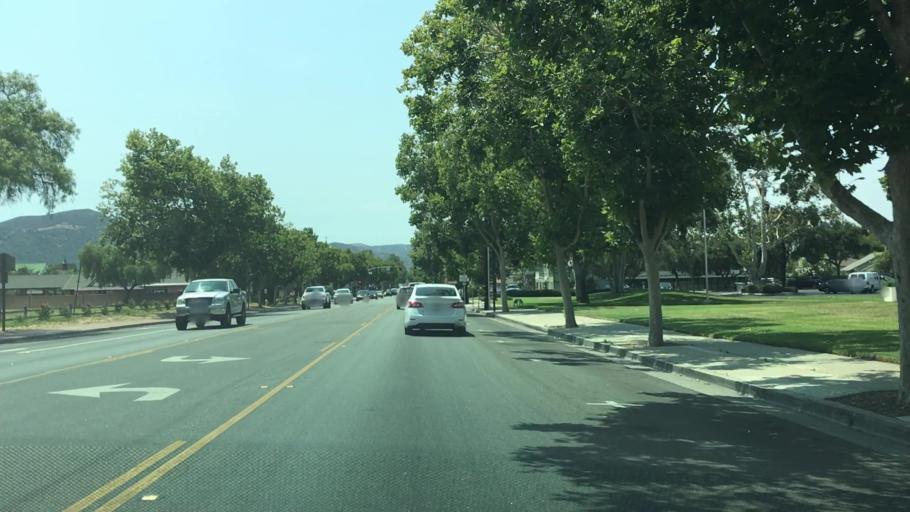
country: US
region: California
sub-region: Santa Barbara County
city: Solvang
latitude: 34.5960
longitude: -120.1356
